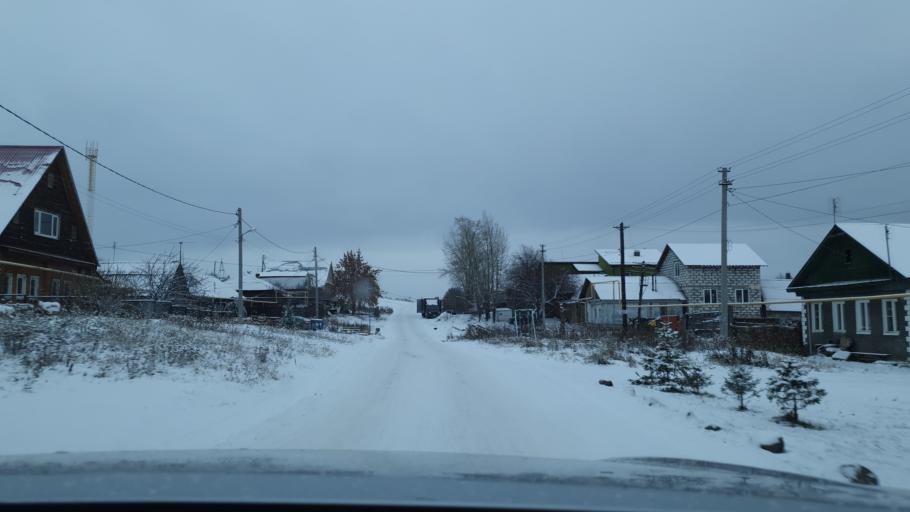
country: RU
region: Sverdlovsk
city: Istok
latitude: 56.7444
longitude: 60.6990
